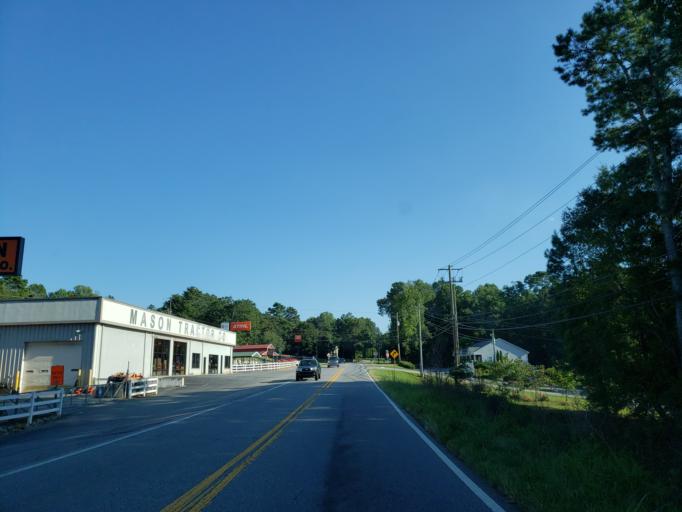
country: US
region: Georgia
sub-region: Forsyth County
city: Cumming
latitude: 34.2585
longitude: -84.1052
